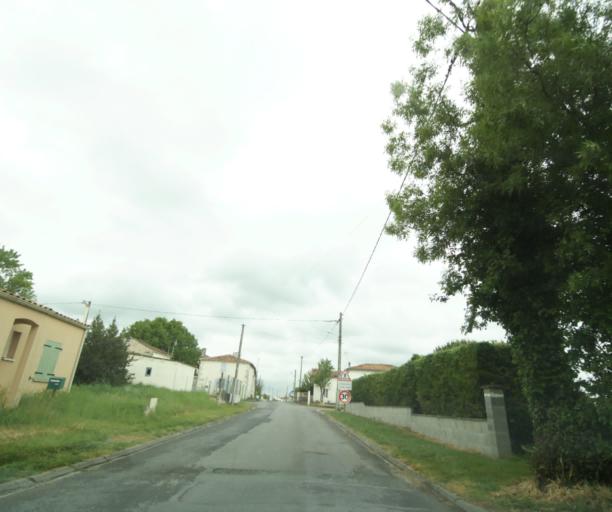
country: FR
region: Poitou-Charentes
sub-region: Departement de la Charente-Maritime
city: Chaniers
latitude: 45.6970
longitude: -0.5146
